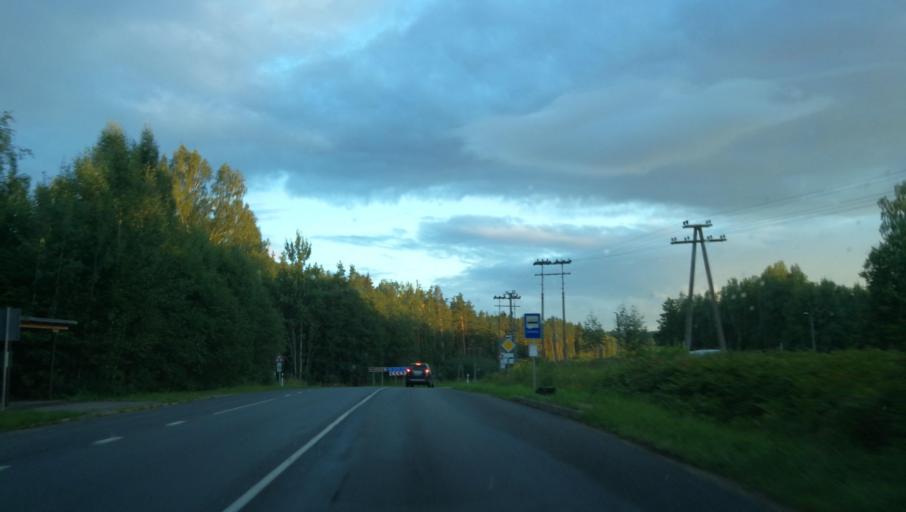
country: LV
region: Priekuli
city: Priekuli
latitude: 57.3658
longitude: 25.3811
